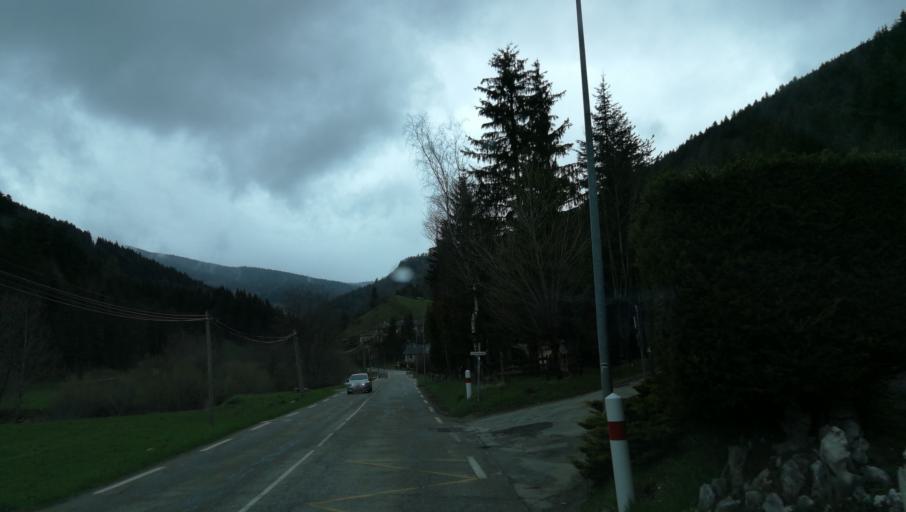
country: FR
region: Rhone-Alpes
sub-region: Departement de l'Isere
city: Villard-de-Lans
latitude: 45.0736
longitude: 5.5399
